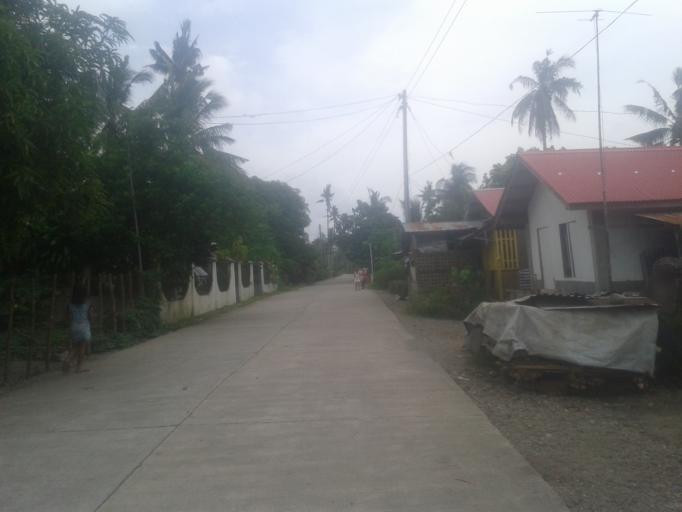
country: PH
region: Eastern Visayas
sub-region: Province of Leyte
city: Mayorga
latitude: 10.8916
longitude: 125.0107
